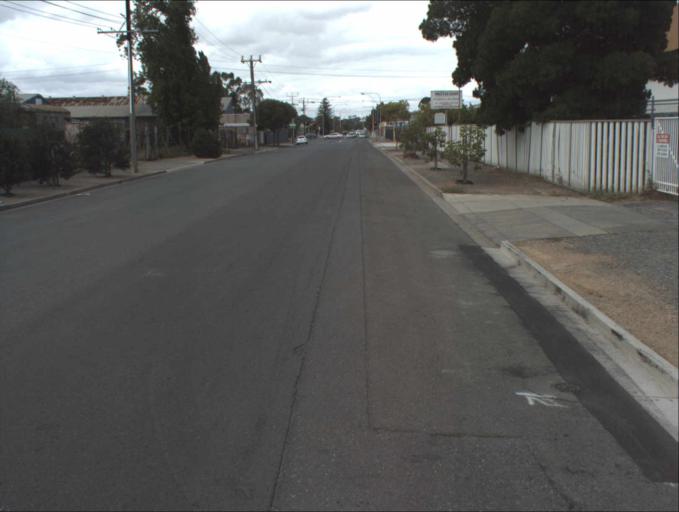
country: AU
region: South Australia
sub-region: Port Adelaide Enfield
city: Enfield
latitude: -34.8471
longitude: 138.5912
